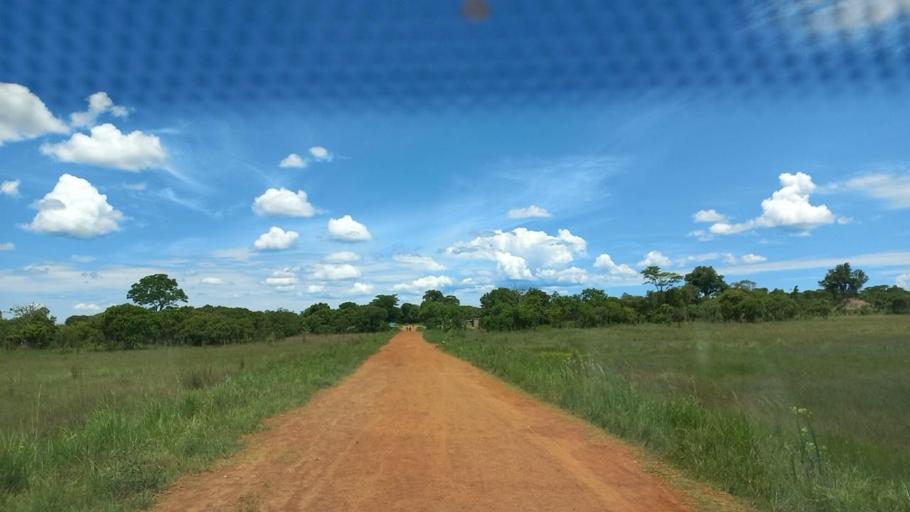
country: ZM
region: North-Western
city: Kabompo
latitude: -12.7491
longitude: 24.2674
